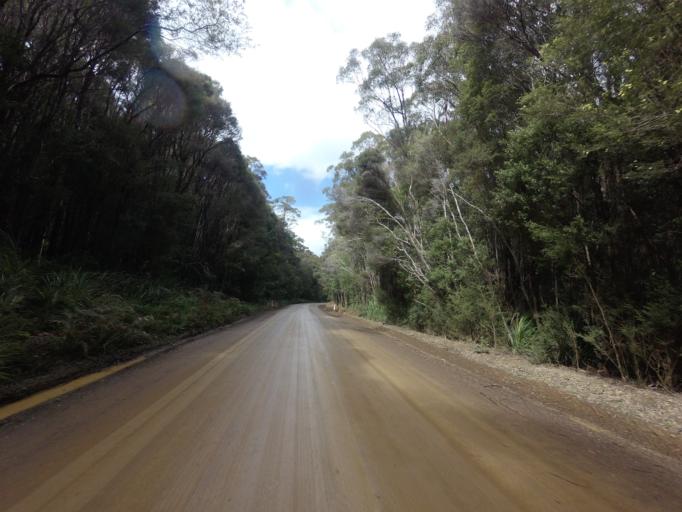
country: AU
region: Tasmania
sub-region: Huon Valley
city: Geeveston
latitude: -43.4086
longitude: 146.8714
